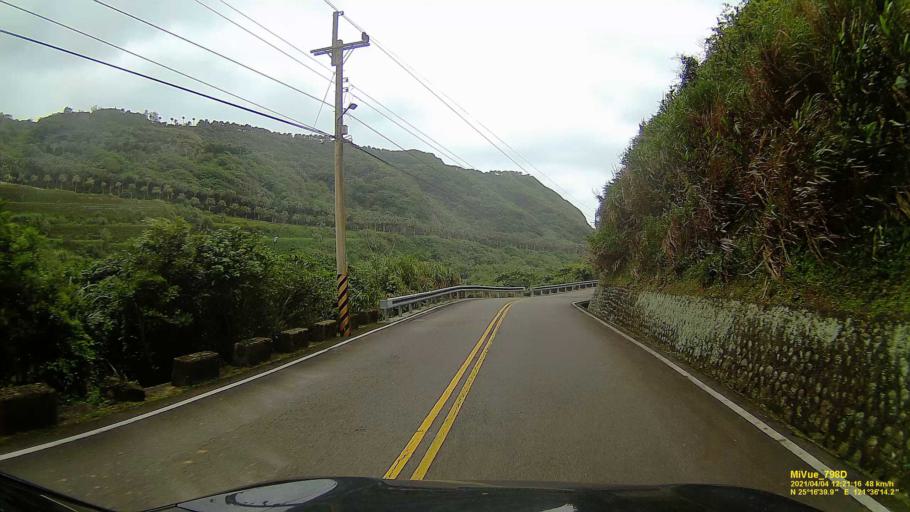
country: TW
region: Taiwan
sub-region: Keelung
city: Keelung
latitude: 25.2782
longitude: 121.6040
